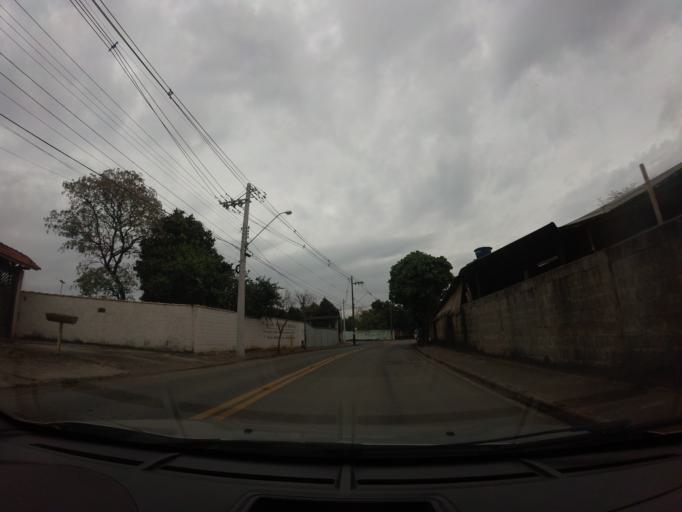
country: BR
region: Sao Paulo
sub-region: Piracicaba
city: Piracicaba
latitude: -22.7449
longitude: -47.5932
